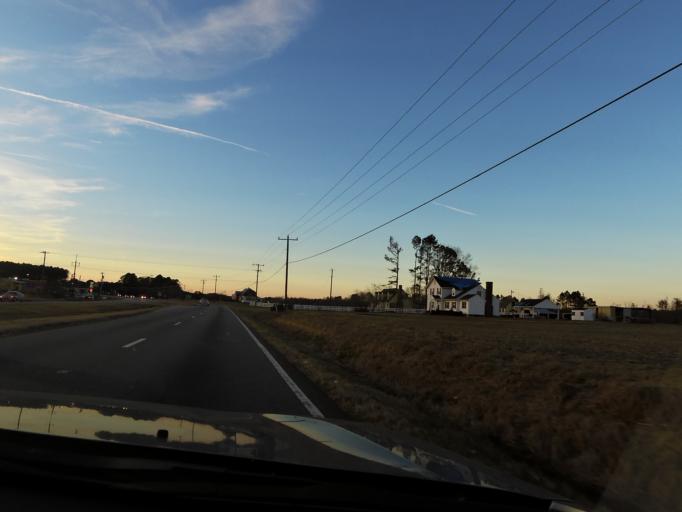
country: US
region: Virginia
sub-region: Southampton County
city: Courtland
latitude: 36.6933
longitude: -77.0324
